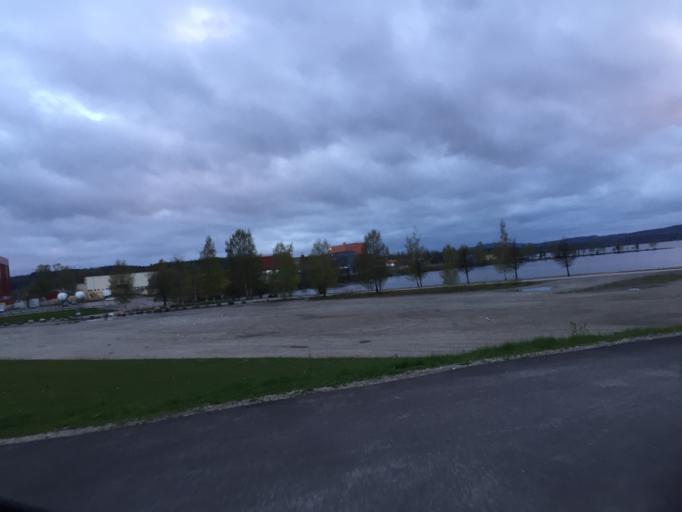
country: SE
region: Dalarna
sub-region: Ludvika Kommun
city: Ludvika
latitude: 60.1496
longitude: 15.1810
